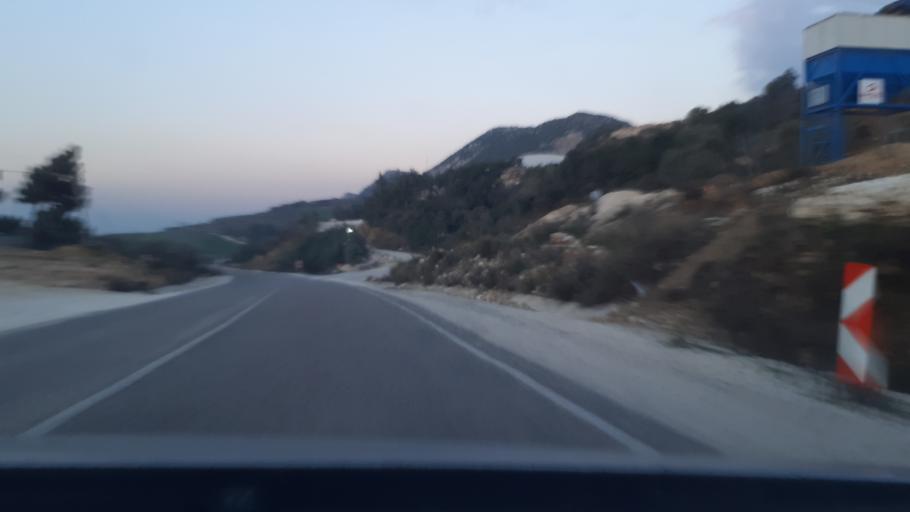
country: TR
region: Hatay
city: Dursunlu
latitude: 36.1746
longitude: 36.1872
